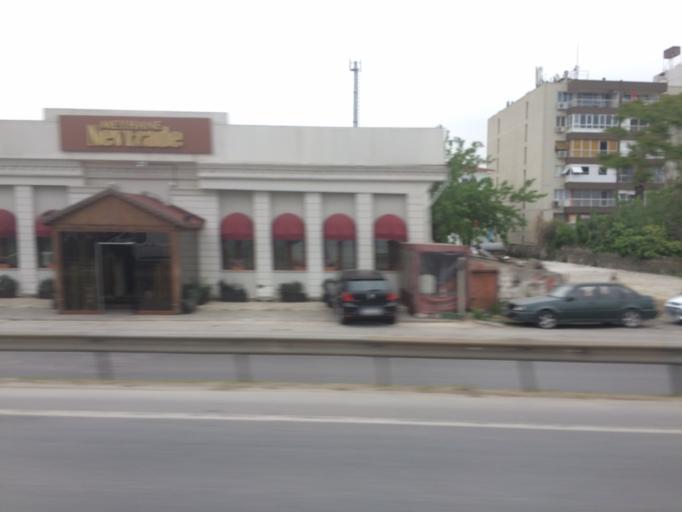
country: TR
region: Izmir
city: Karsiyaka
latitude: 38.4623
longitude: 27.1640
